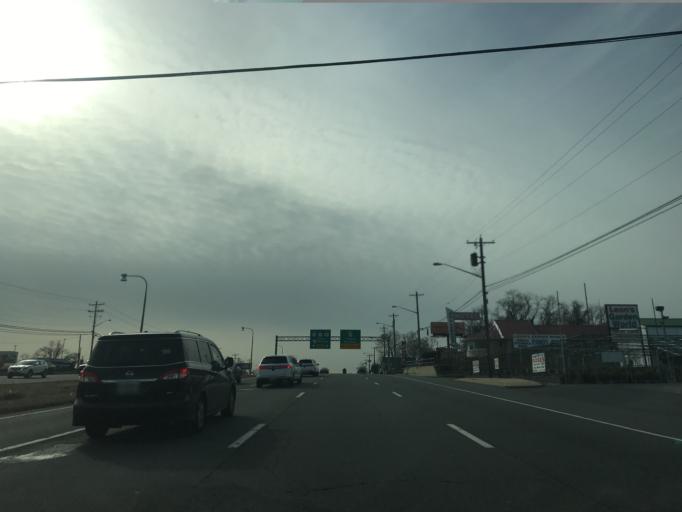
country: US
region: Delaware
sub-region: New Castle County
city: Wilmington Manor
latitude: 39.6618
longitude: -75.6084
